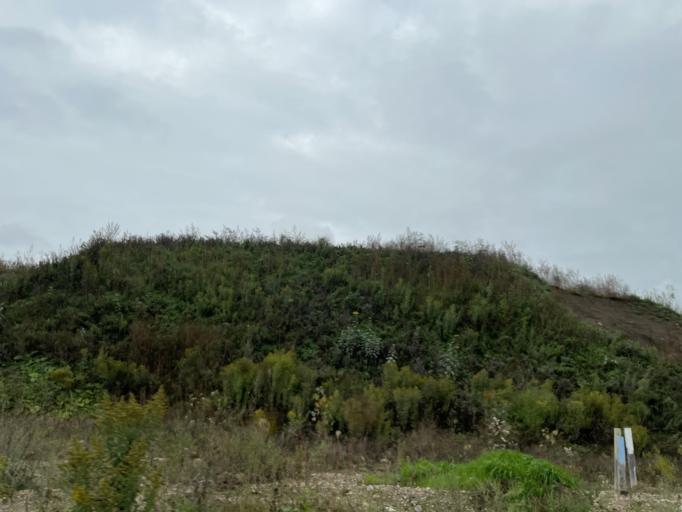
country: CA
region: Ontario
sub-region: Wellington County
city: Guelph
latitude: 43.5254
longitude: -80.1995
